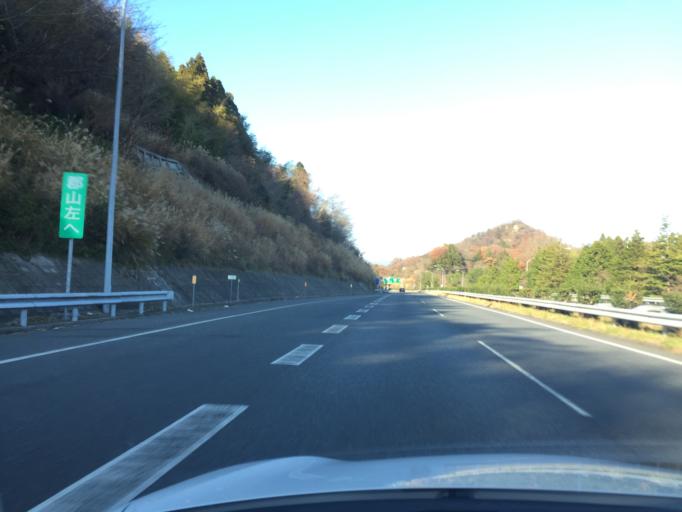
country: JP
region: Fukushima
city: Iwaki
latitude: 37.0223
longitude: 140.8134
